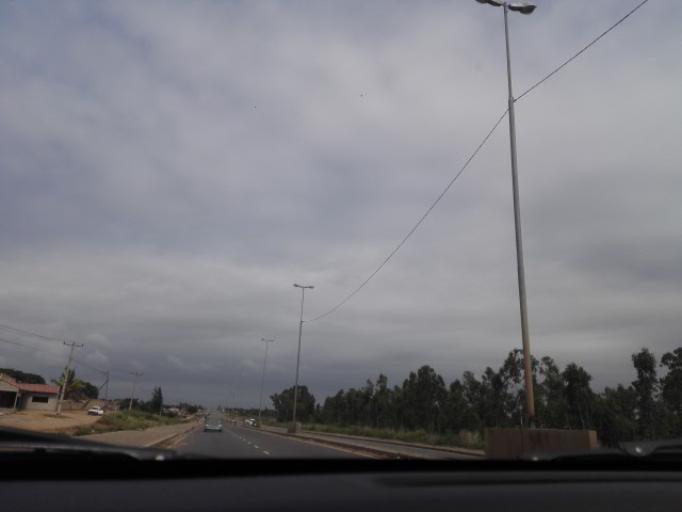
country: MZ
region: Maputo City
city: Maputo
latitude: -25.8295
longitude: 32.6113
